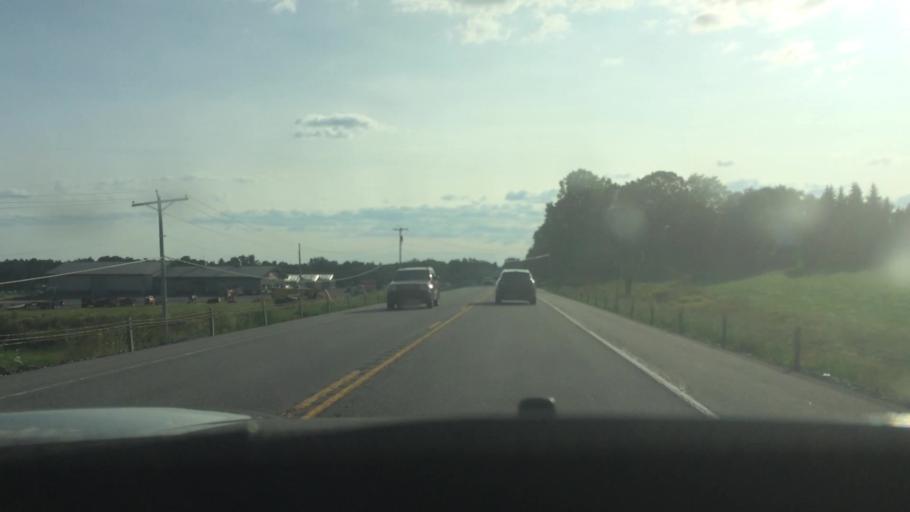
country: US
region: New York
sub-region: St. Lawrence County
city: Canton
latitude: 44.6146
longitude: -75.1120
